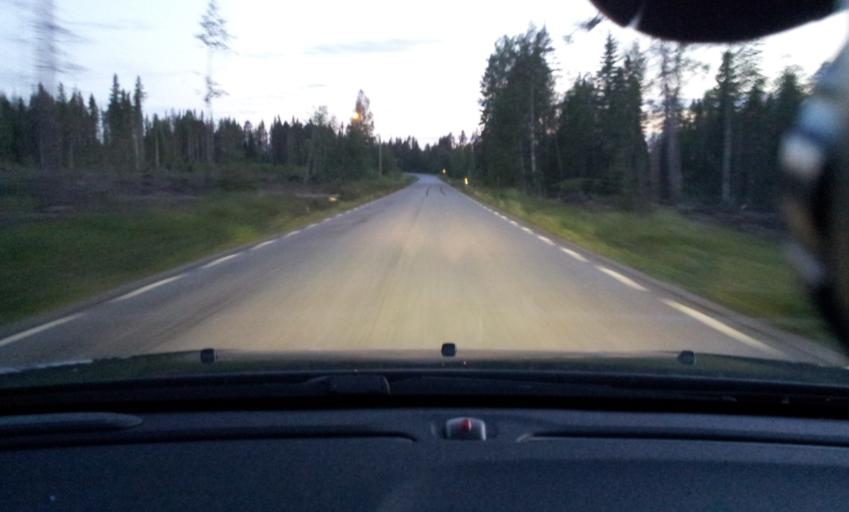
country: SE
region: Jaemtland
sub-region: Braecke Kommun
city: Braecke
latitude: 62.7639
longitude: 15.3066
